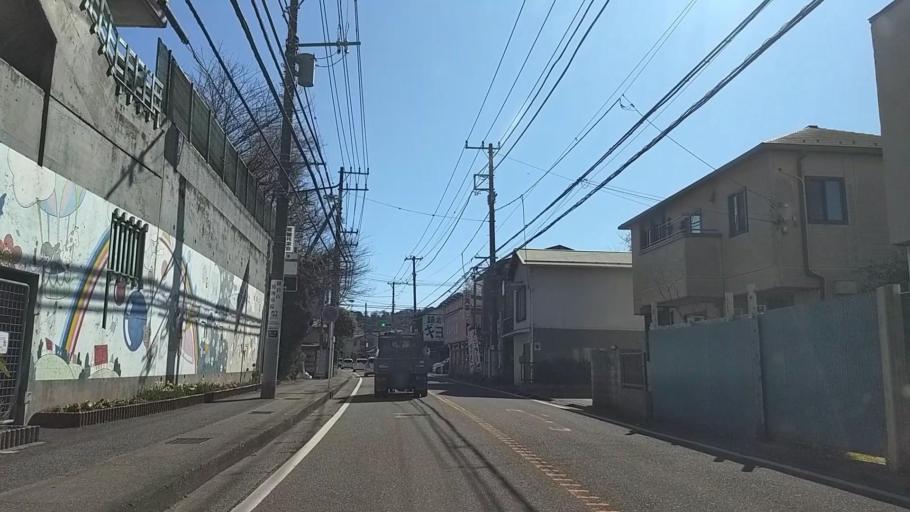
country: JP
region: Kanagawa
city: Kamakura
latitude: 35.3240
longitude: 139.5248
